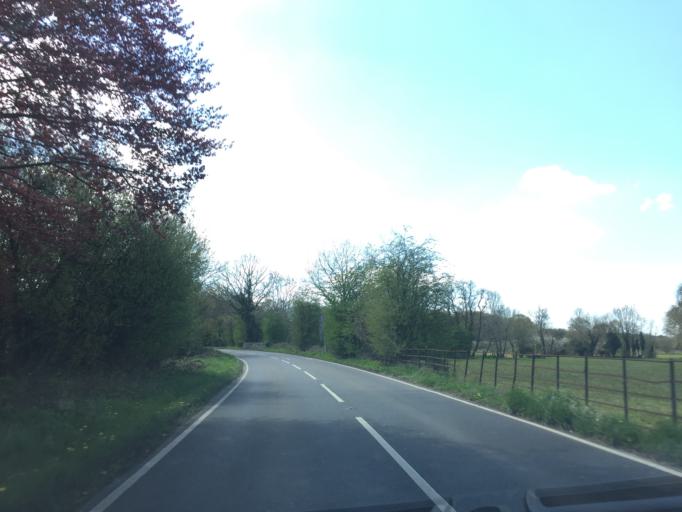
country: GB
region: England
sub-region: East Sussex
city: Crowborough
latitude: 51.1084
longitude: 0.1125
